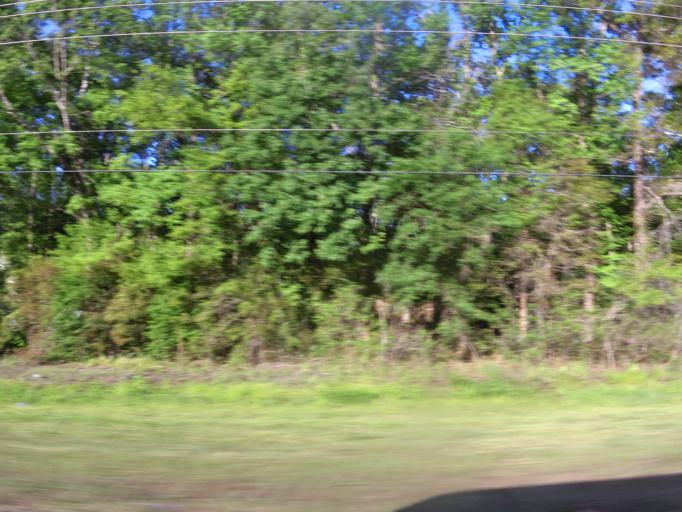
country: US
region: Florida
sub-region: Saint Johns County
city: Palm Valley
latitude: 30.0573
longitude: -81.4323
